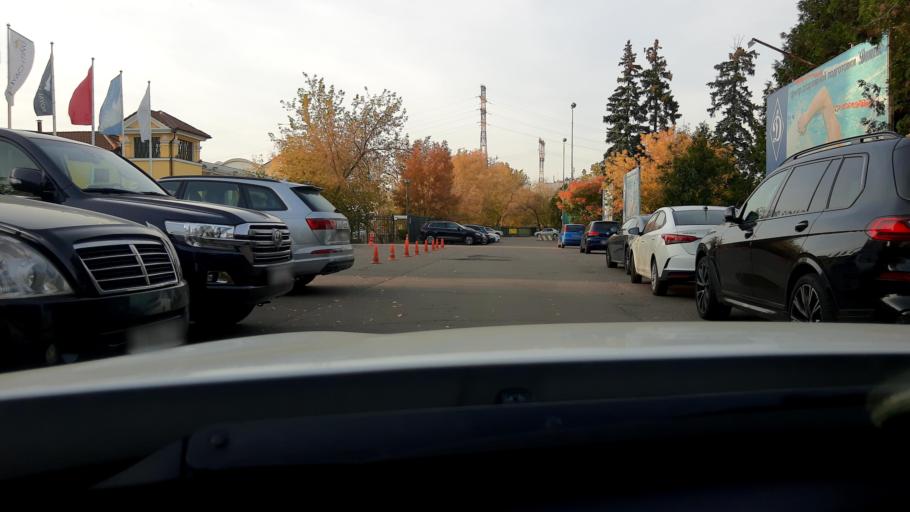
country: RU
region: Moskovskaya
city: Levoberezhnyy
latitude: 55.8349
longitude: 37.4806
